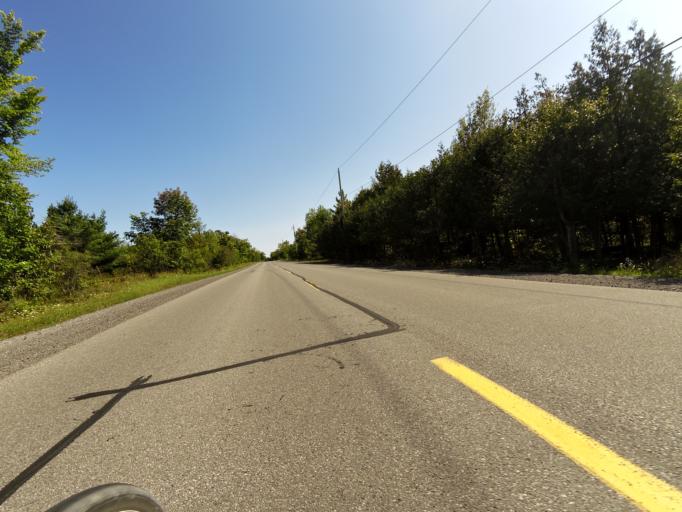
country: CA
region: Ontario
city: Bells Corners
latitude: 45.4281
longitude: -75.9566
